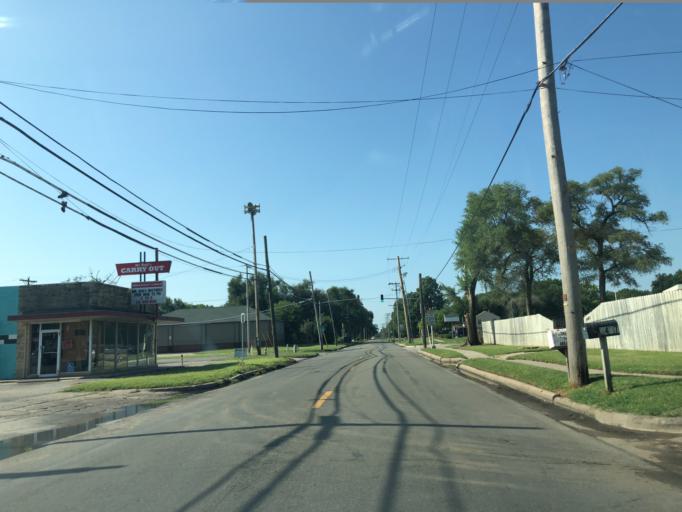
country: US
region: Kansas
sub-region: Sedgwick County
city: Wichita
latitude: 37.7457
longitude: -97.3449
